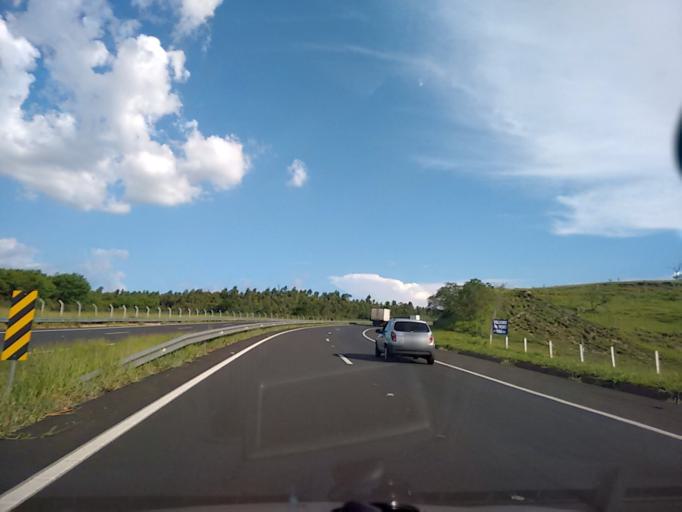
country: BR
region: Sao Paulo
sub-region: Duartina
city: Duartina
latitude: -22.3220
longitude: -49.4771
